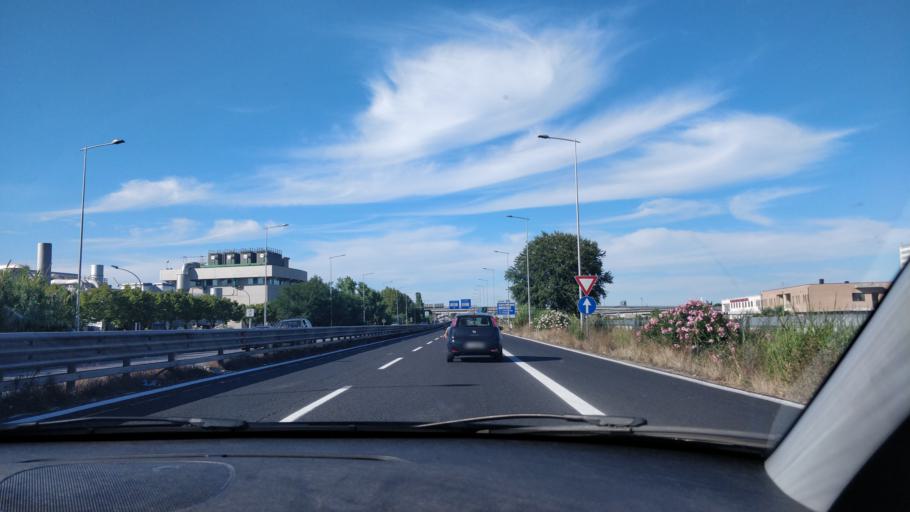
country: IT
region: Abruzzo
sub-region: Provincia di Pescara
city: Villa Raspa
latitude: 42.4410
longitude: 14.1859
